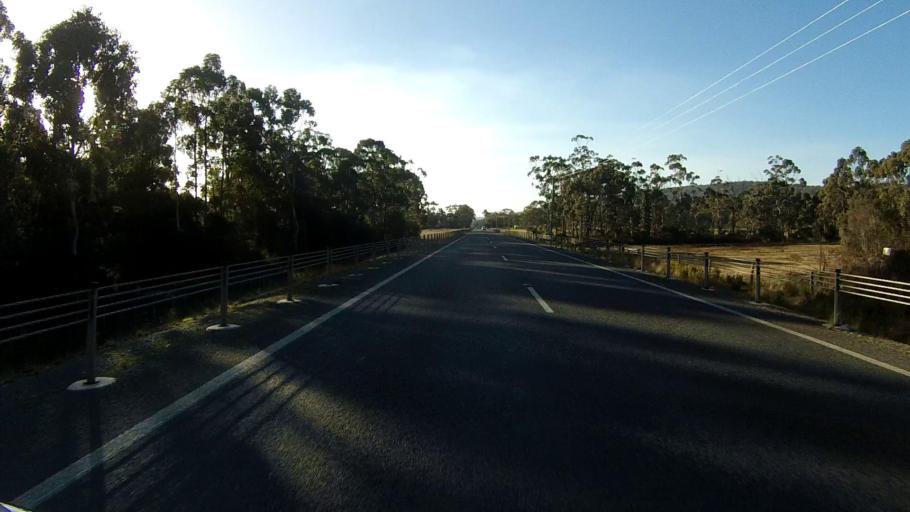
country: AU
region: Tasmania
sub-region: Clarence
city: Sandford
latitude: -43.0729
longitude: 147.8630
